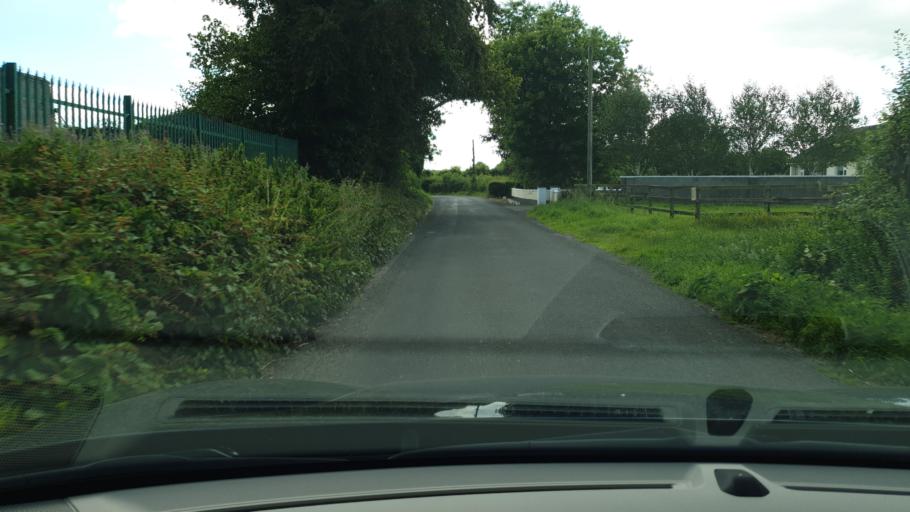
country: IE
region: Leinster
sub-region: An Mhi
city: Dunboyne
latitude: 53.4077
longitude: -6.4910
